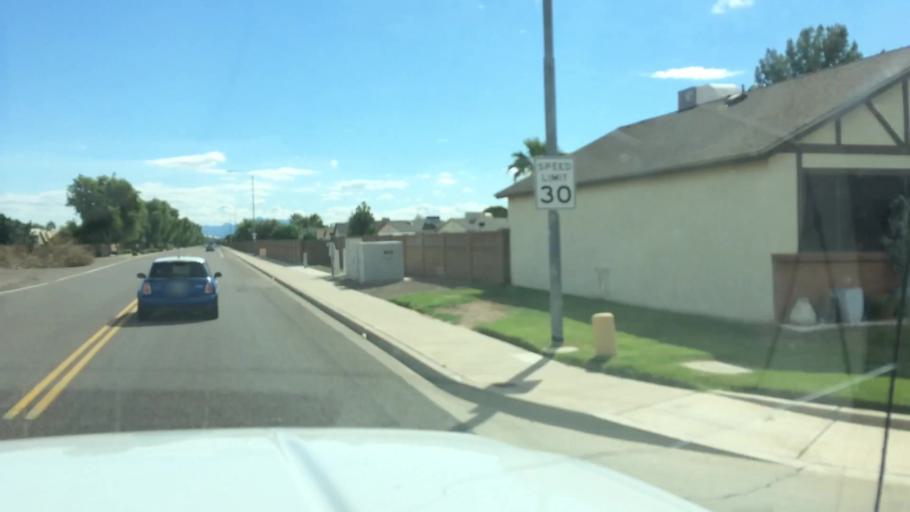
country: US
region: Arizona
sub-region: Maricopa County
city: Sun City
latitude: 33.5797
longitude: -112.2639
